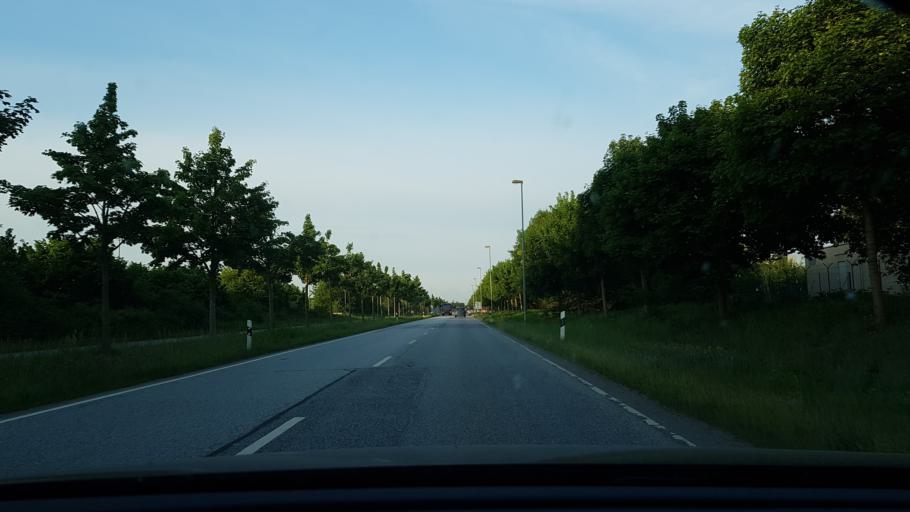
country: DE
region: Schleswig-Holstein
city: Luebeck
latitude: 53.8391
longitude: 10.6548
